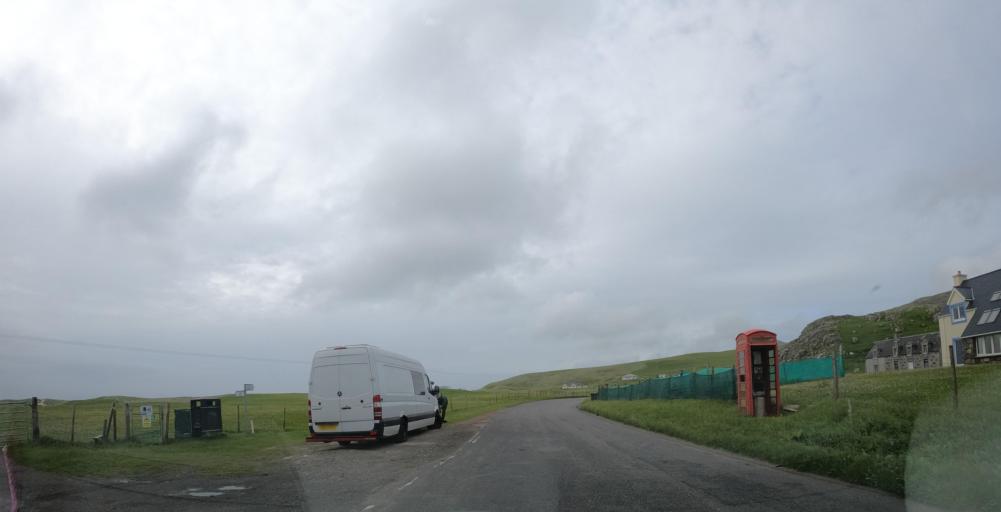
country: GB
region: Scotland
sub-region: Eilean Siar
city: Barra
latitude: 56.9703
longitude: -7.5168
